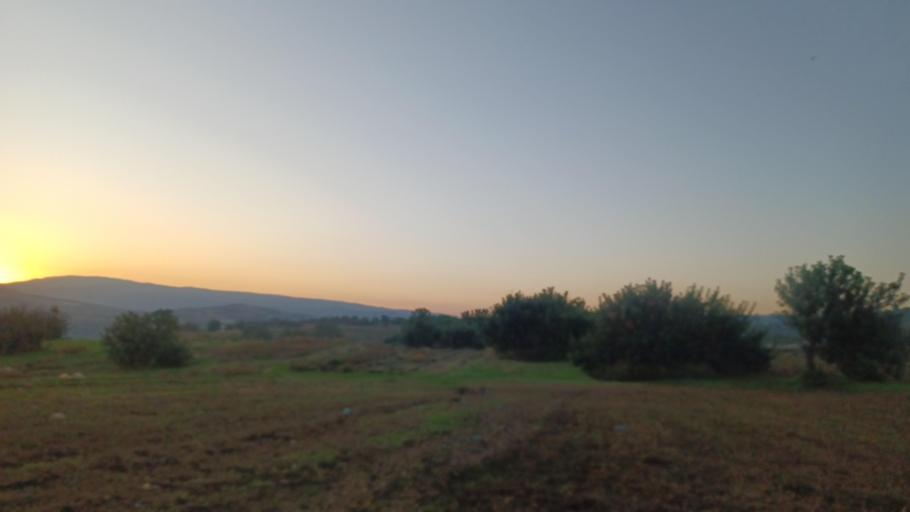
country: CY
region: Pafos
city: Polis
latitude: 34.9863
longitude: 32.4372
